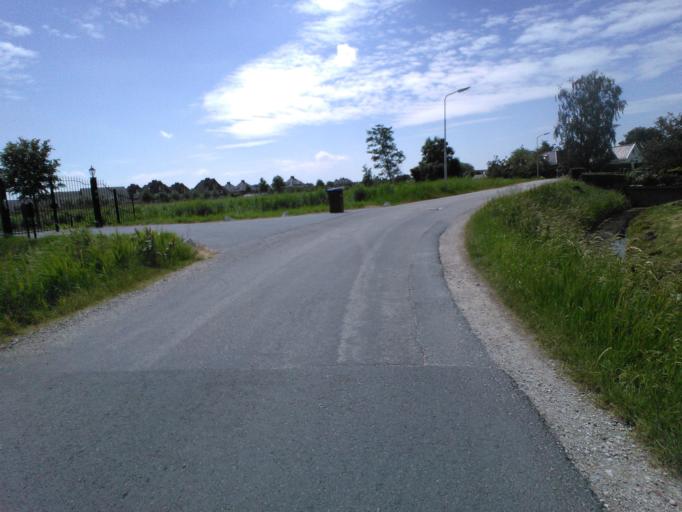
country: NL
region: South Holland
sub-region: Gemeente Alblasserdam
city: Alblasserdam
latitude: 51.8661
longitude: 4.6776
